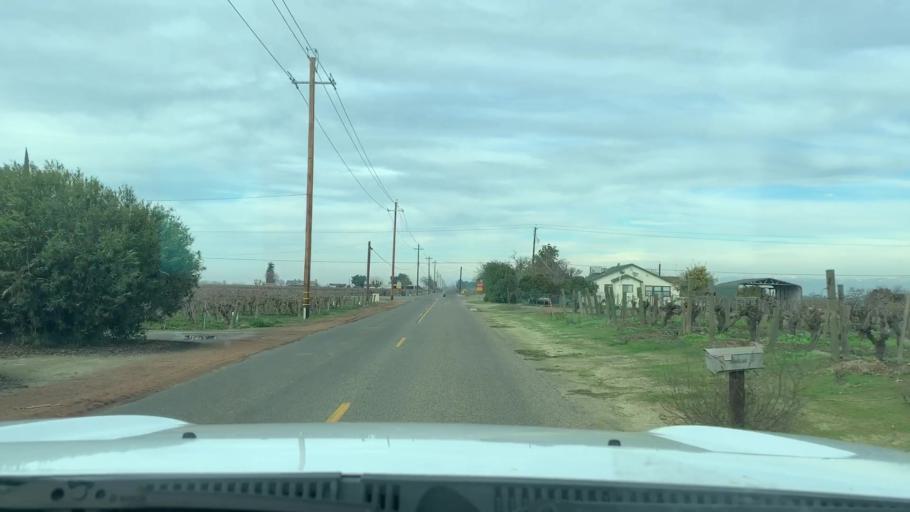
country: US
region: California
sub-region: Fresno County
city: Selma
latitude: 36.5676
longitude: -119.5750
